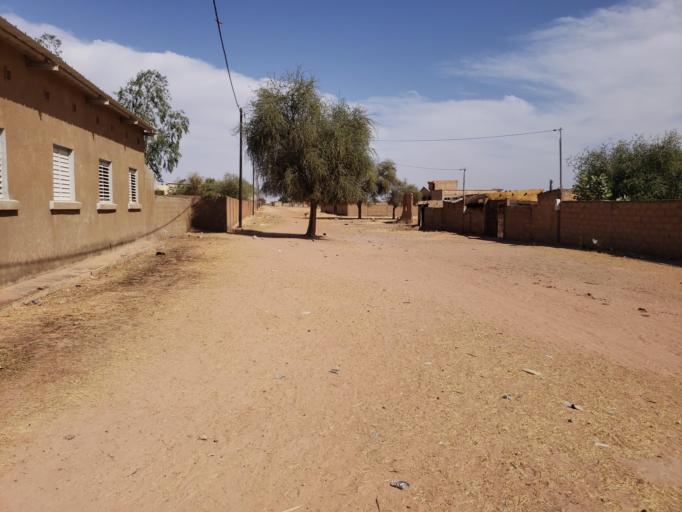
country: SN
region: Matam
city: Ranerou
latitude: 15.2998
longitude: -13.9678
